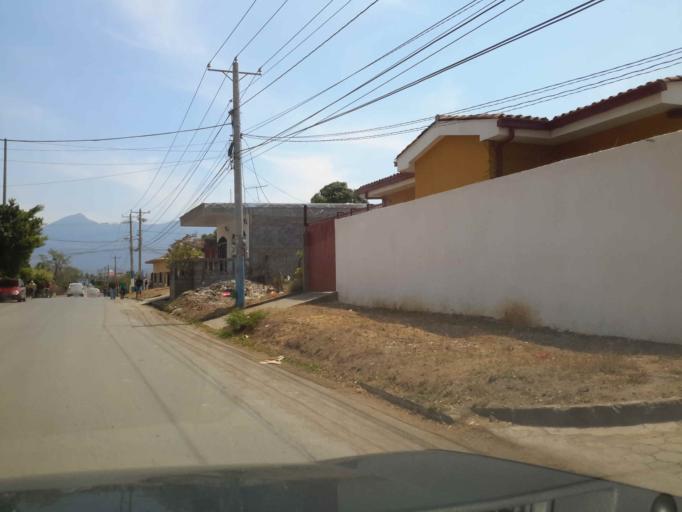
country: NI
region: Granada
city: Granada
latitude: 11.9401
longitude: -85.9621
